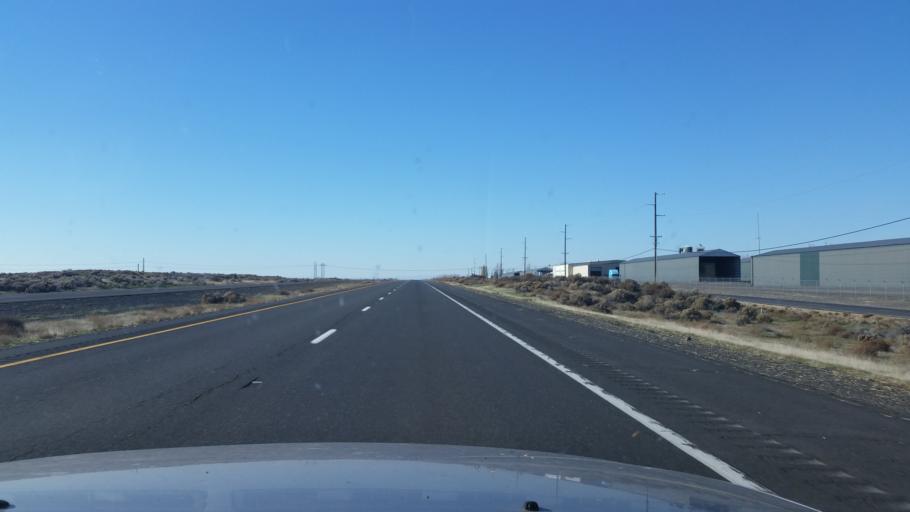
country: US
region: Washington
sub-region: Grant County
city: Cascade Valley
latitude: 47.1042
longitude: -119.3841
